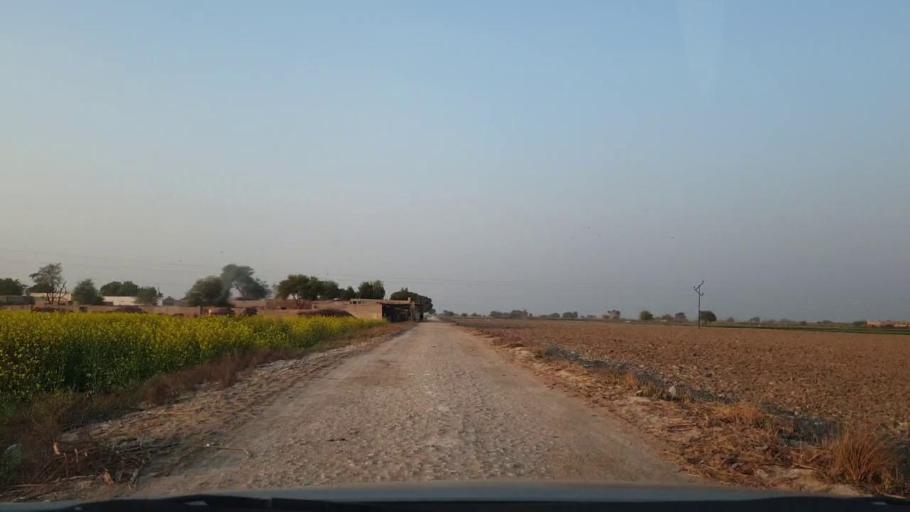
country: PK
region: Sindh
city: Tando Adam
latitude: 25.7116
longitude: 68.5792
